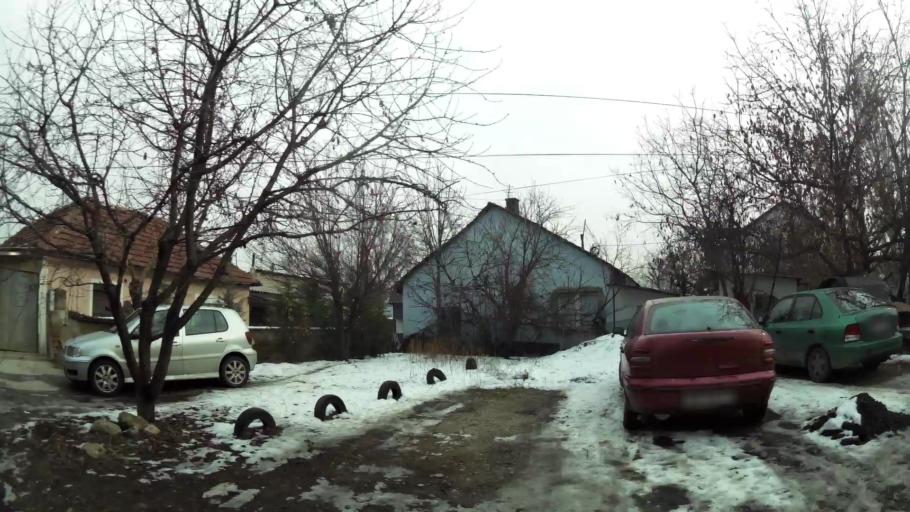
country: MK
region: Cair
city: Cair
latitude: 41.9958
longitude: 21.4578
